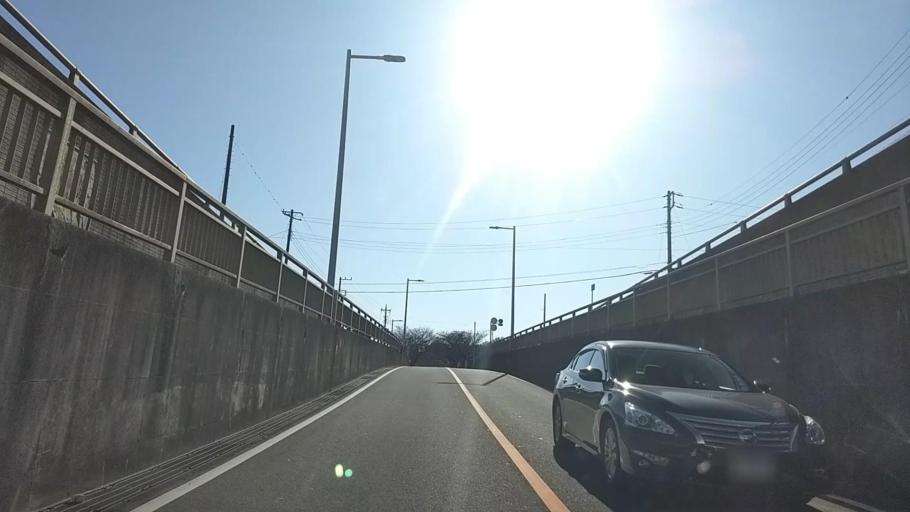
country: JP
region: Kanagawa
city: Hadano
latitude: 35.3705
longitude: 139.2043
